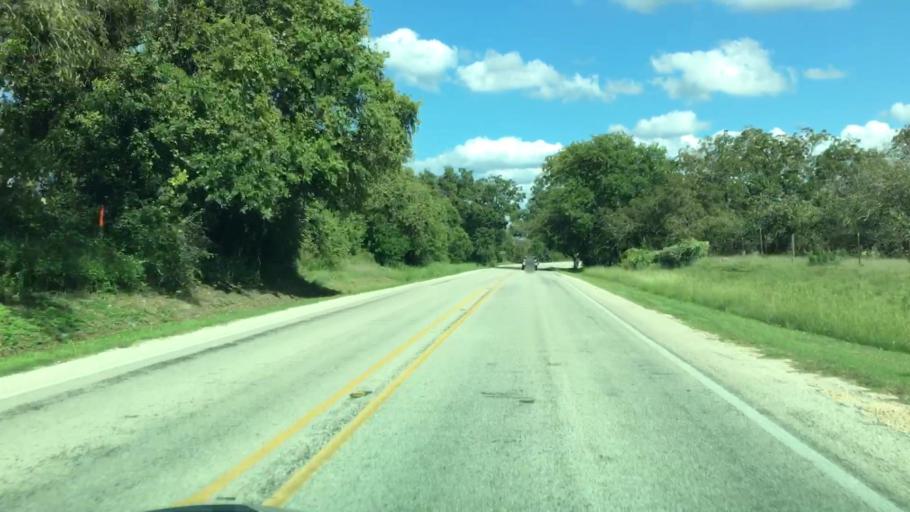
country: US
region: Texas
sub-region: Blanco County
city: Blanco
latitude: 30.0929
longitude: -98.4107
